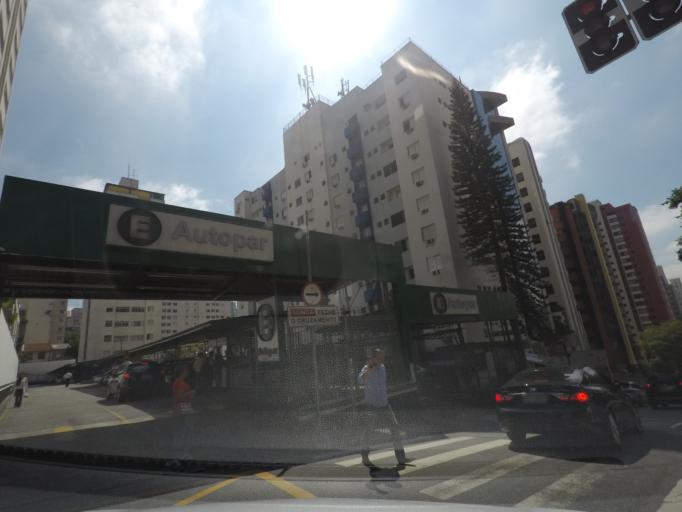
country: BR
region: Sao Paulo
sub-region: Sao Paulo
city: Sao Paulo
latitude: -23.5569
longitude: -46.6548
